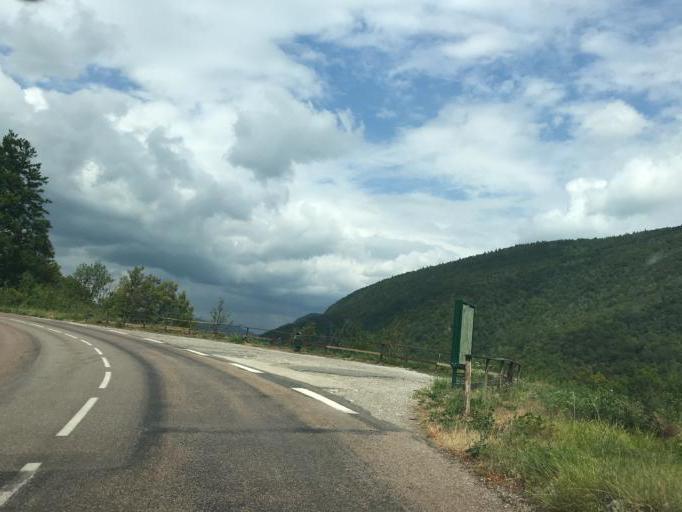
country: FR
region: Franche-Comte
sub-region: Departement du Jura
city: Valfin-les-Saint-Claude
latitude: 46.4269
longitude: 5.8588
